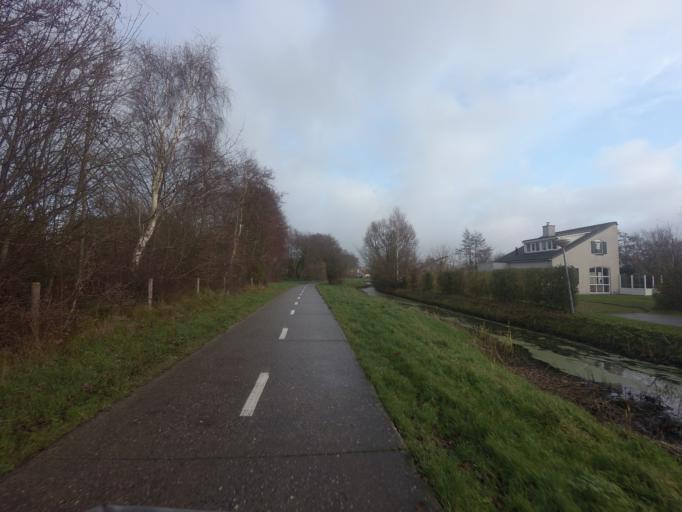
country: NL
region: North Holland
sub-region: Gemeente Texel
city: Den Burg
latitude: 53.1549
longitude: 4.8471
